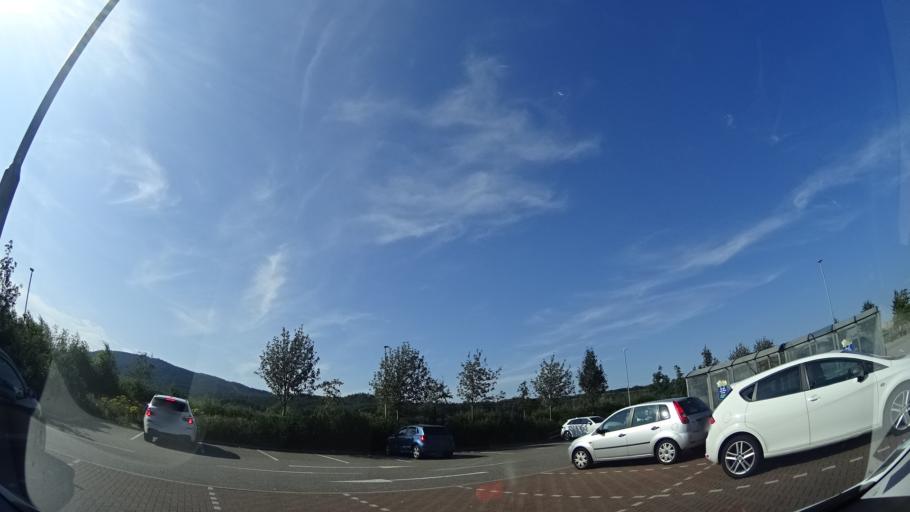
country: GB
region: Scotland
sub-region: Highland
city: Inverness
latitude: 57.4520
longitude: -4.2511
